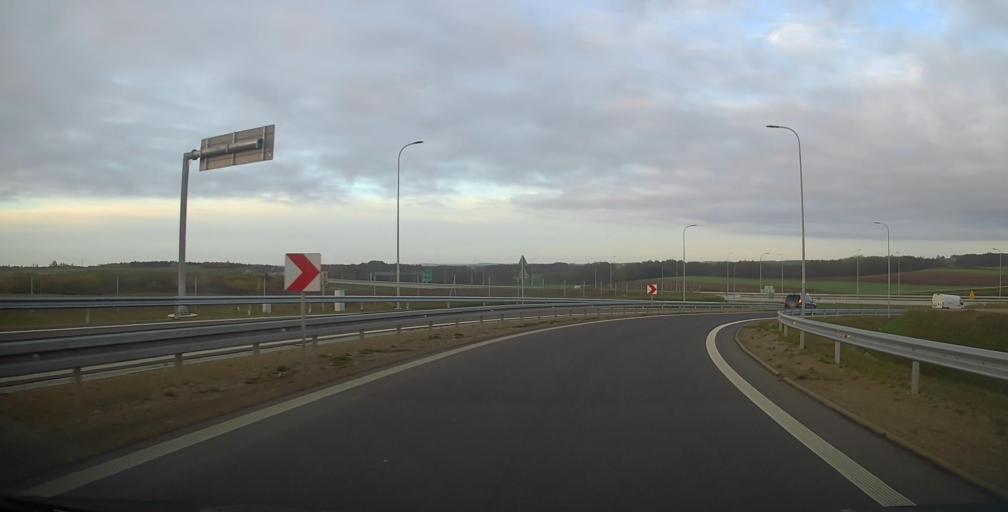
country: PL
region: Podlasie
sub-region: Powiat lomzynski
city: Piatnica
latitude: 53.2488
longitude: 22.1067
